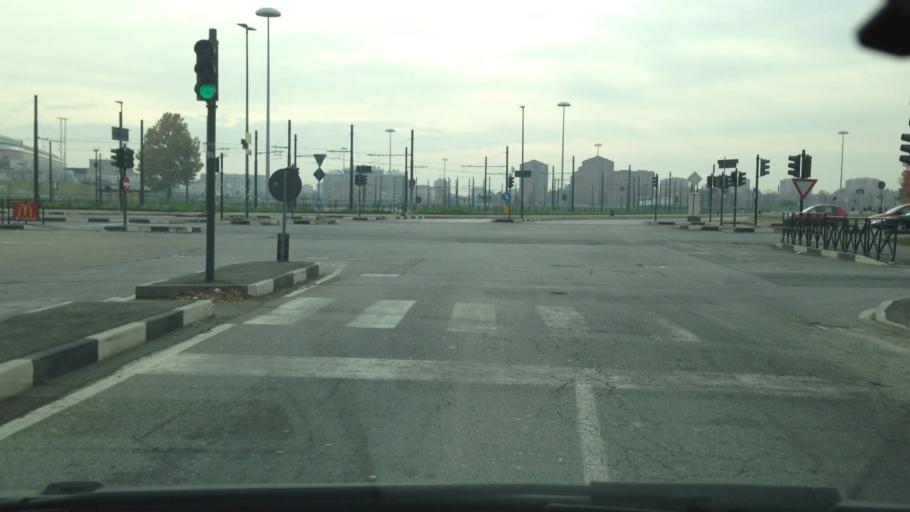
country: IT
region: Piedmont
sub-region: Provincia di Torino
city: Venaria Reale
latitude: 45.1129
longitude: 7.6378
